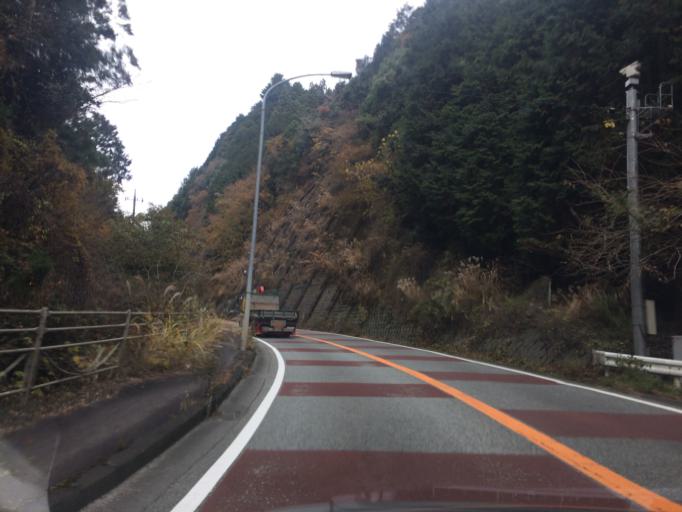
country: JP
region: Shizuoka
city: Fujinomiya
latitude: 35.2024
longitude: 138.5177
